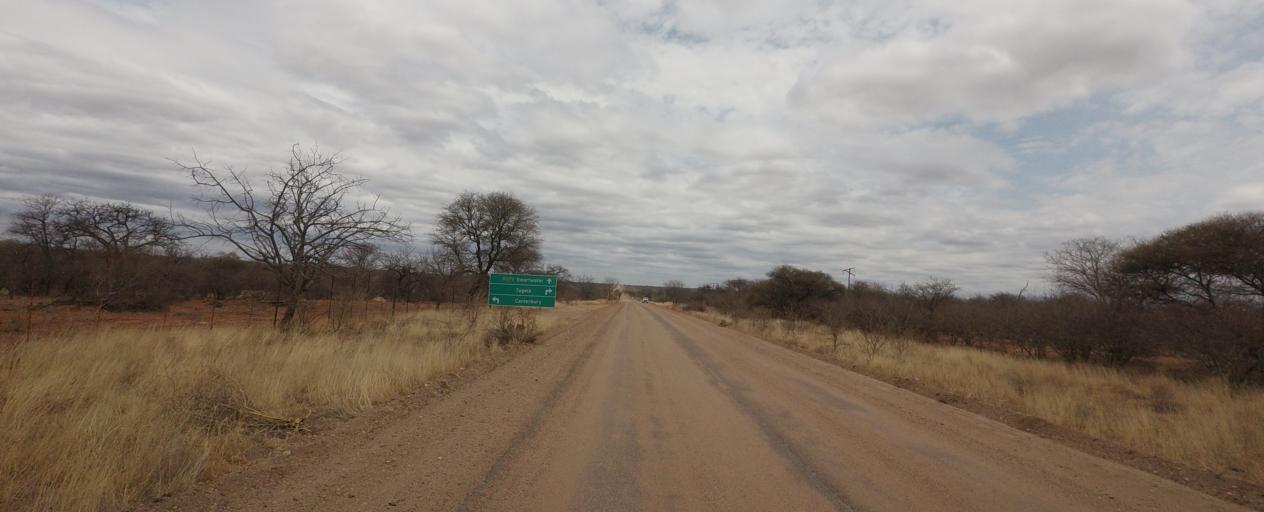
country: BW
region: Central
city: Mathathane
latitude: -22.6808
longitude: 28.6597
